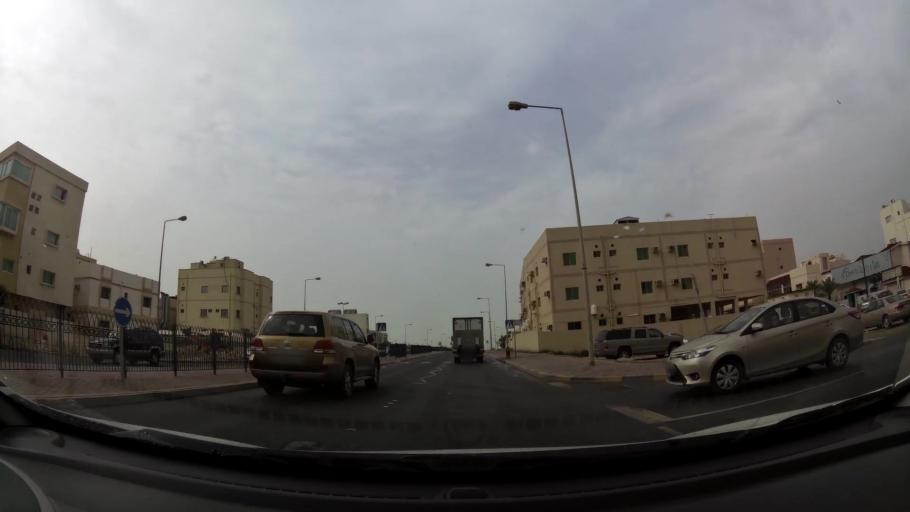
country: BH
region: Northern
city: Ar Rifa'
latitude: 26.1334
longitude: 50.5613
